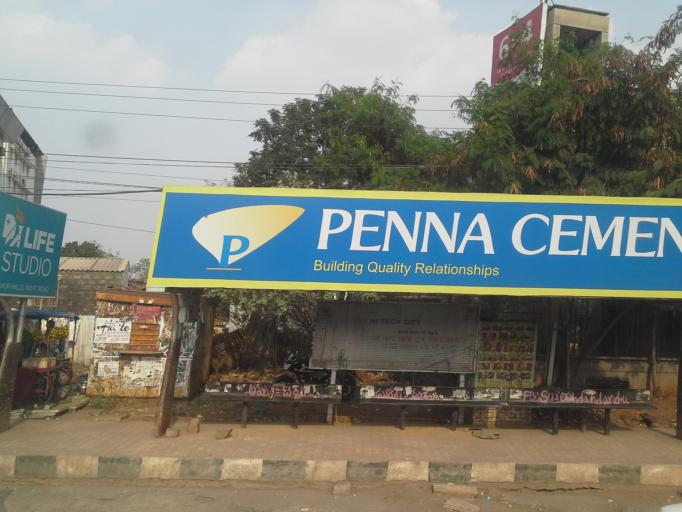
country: IN
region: Telangana
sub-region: Rangareddi
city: Kukatpalli
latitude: 17.4500
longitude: 78.3825
